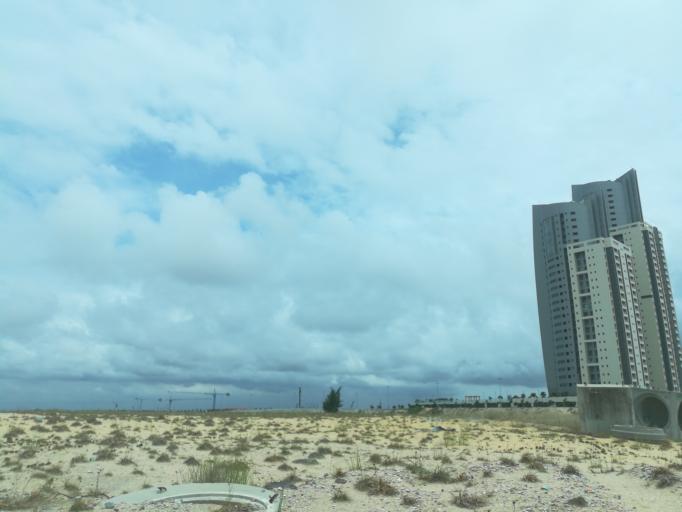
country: NG
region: Lagos
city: Lagos
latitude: 6.4063
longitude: 3.4102
